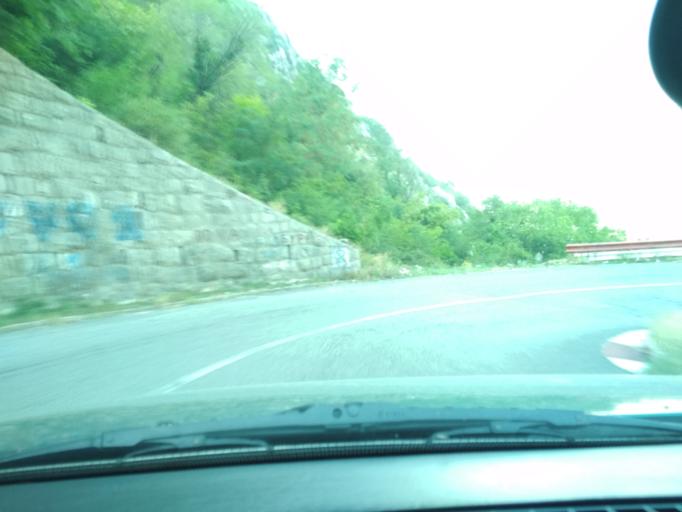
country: ME
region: Kotor
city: Kotor
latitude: 42.4064
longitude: 18.7643
